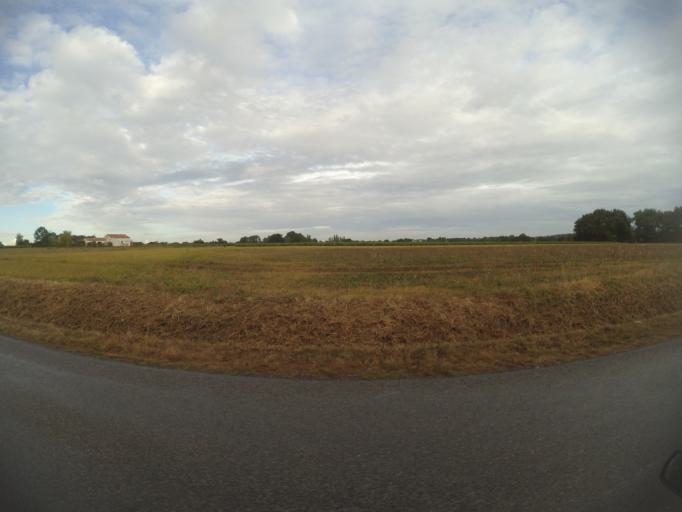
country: FR
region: Pays de la Loire
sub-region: Departement de la Loire-Atlantique
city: Aigrefeuille-sur-Maine
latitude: 47.0627
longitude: -1.4078
